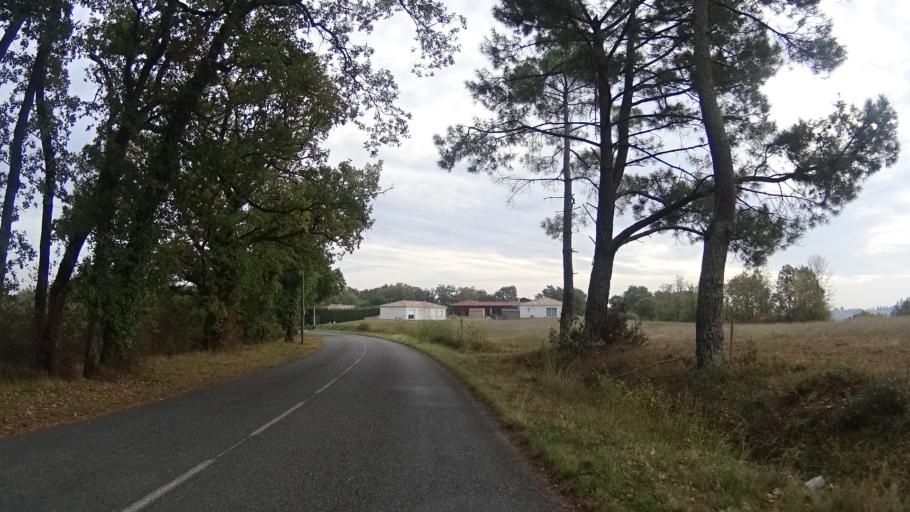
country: FR
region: Aquitaine
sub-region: Departement du Lot-et-Garonne
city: Estillac
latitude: 44.1202
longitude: 0.5917
